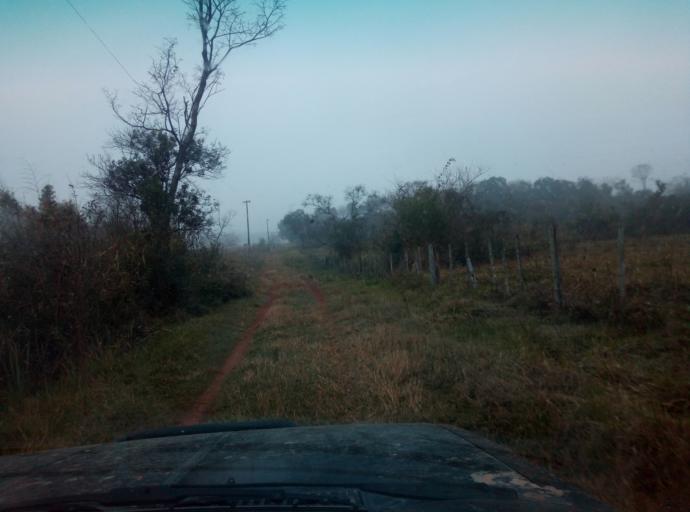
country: PY
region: Caaguazu
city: Doctor Cecilio Baez
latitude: -25.1560
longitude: -56.2613
